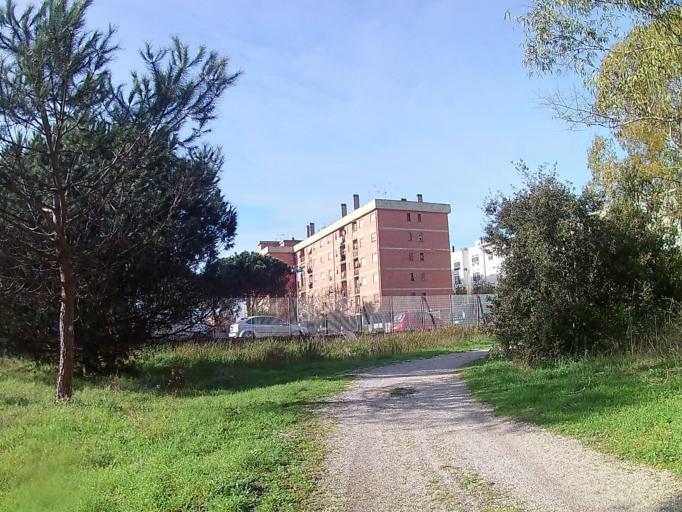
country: IT
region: Latium
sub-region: Citta metropolitana di Roma Capitale
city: Lido di Ostia
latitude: 41.7421
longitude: 12.2654
